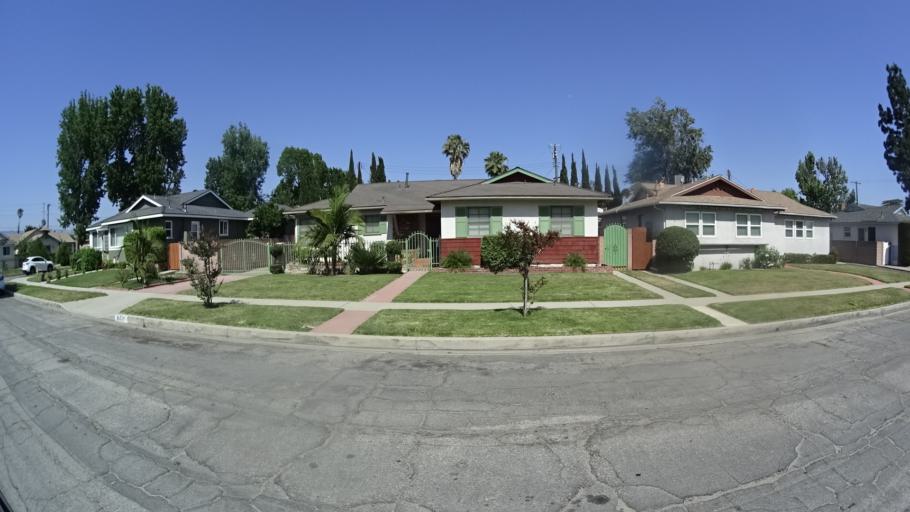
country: US
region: California
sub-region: Los Angeles County
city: Van Nuys
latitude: 34.2203
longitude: -118.4203
